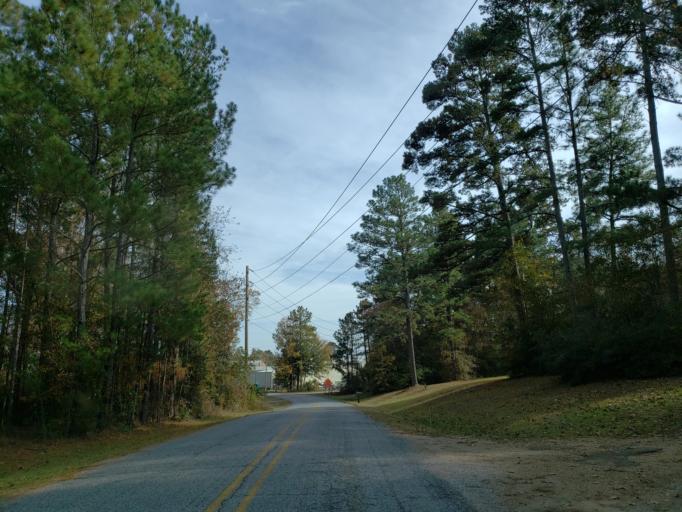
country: US
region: Mississippi
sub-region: Forrest County
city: Rawls Springs
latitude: 31.3712
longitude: -89.3621
